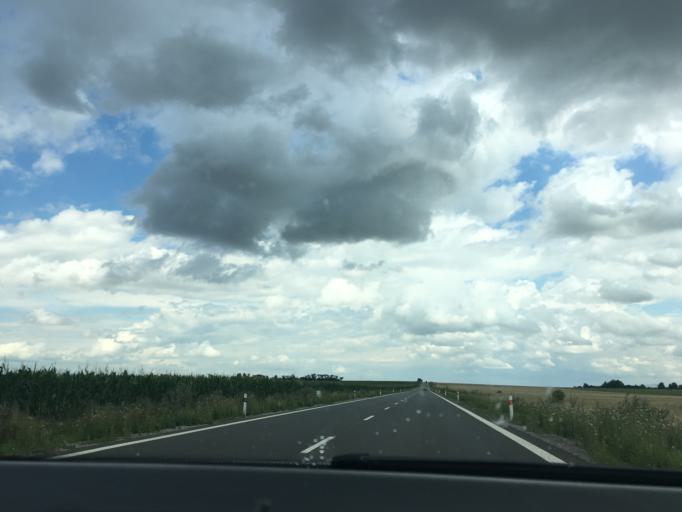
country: SK
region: Kosicky
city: Trebisov
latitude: 48.5627
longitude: 21.6986
